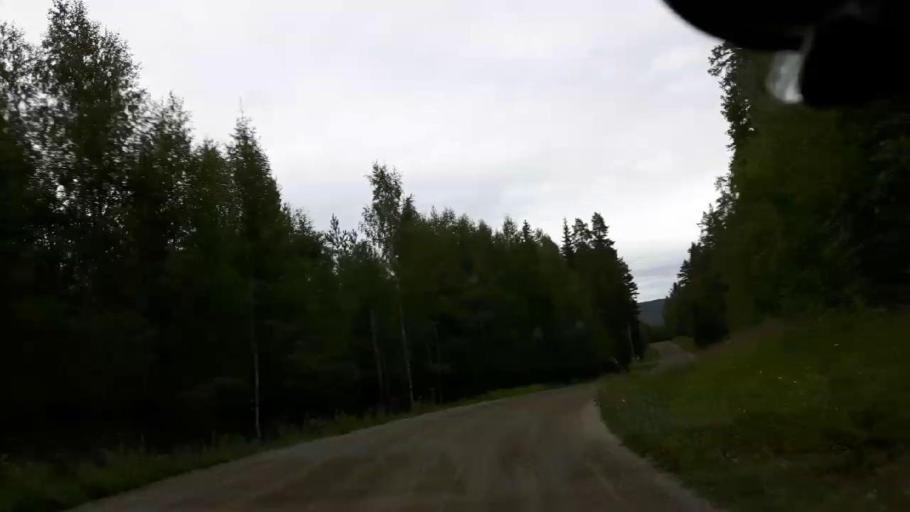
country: SE
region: Jaemtland
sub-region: Braecke Kommun
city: Braecke
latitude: 62.9127
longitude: 15.5830
